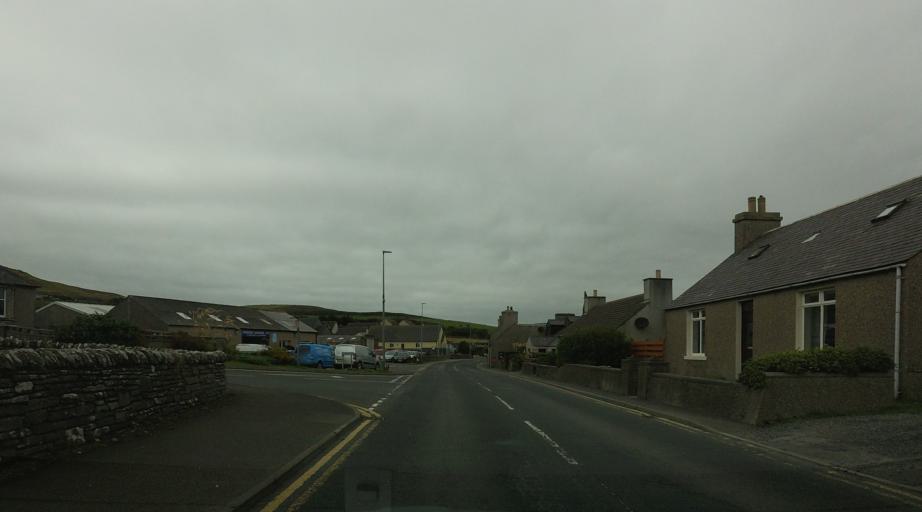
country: GB
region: Scotland
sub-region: Orkney Islands
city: Orkney
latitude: 59.0039
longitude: -3.1099
